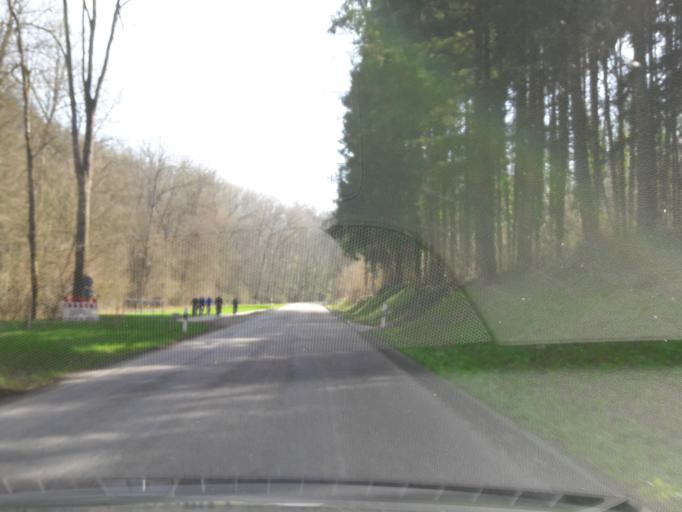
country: DE
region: Baden-Wuerttemberg
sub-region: Regierungsbezirk Stuttgart
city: Ohringen
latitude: 49.2189
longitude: 9.4670
